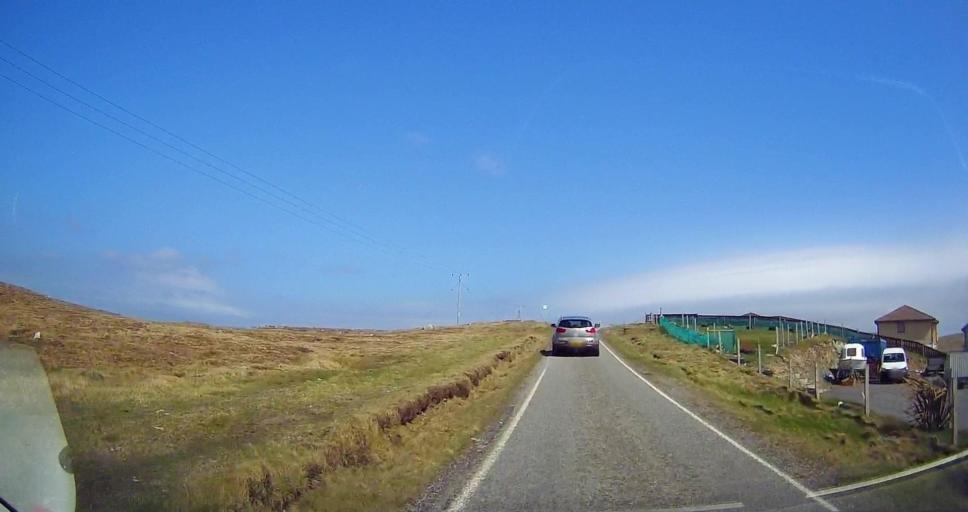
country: GB
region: Scotland
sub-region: Shetland Islands
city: Sandwick
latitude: 60.0879
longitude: -1.3297
